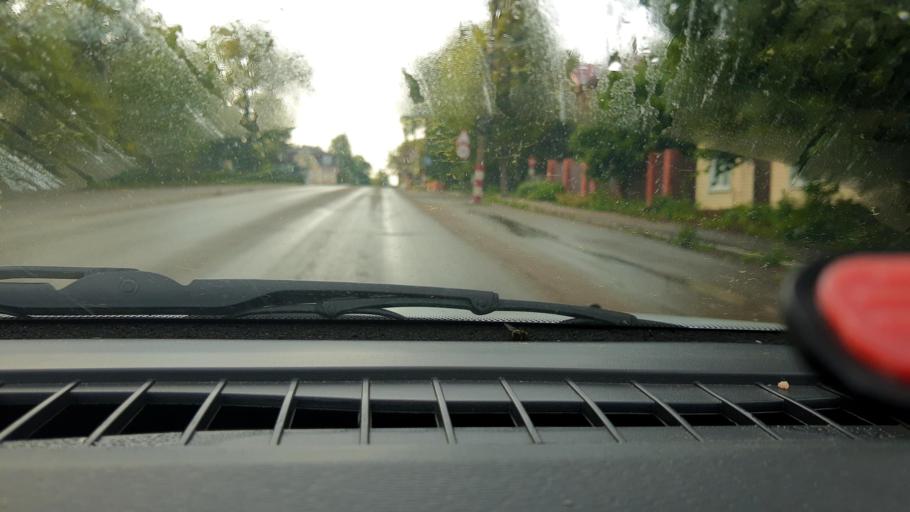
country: RU
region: Nizjnij Novgorod
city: Lukoyanov
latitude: 55.0344
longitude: 44.4948
